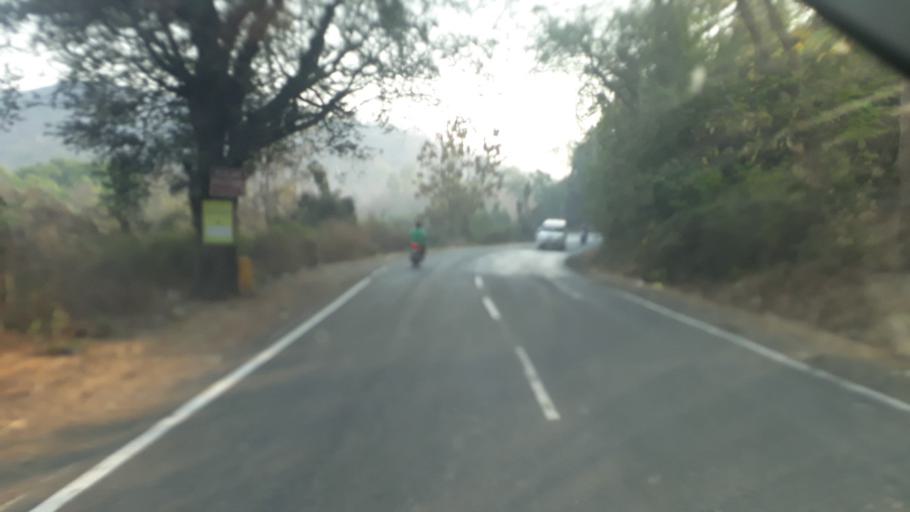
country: IN
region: Maharashtra
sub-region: Raigarh
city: Karjat
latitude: 18.9147
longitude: 73.3001
